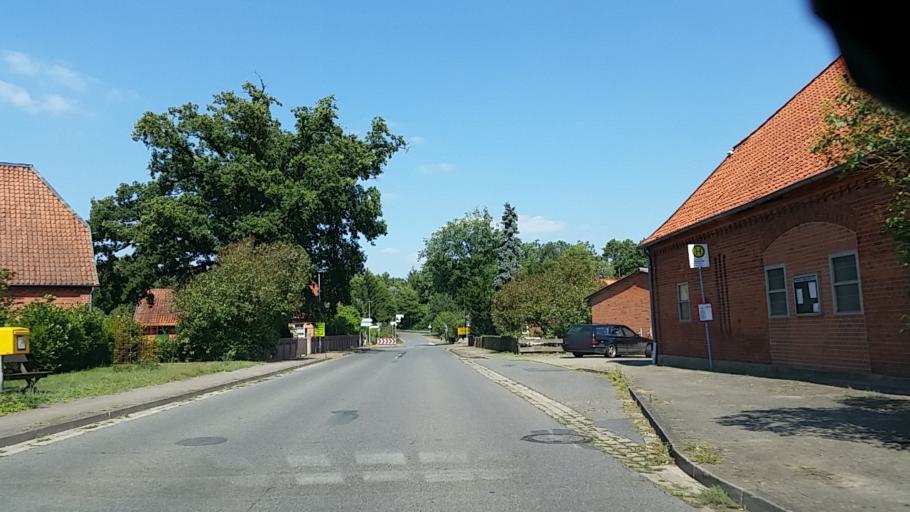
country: DE
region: Lower Saxony
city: Jelmstorf
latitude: 53.1074
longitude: 10.5432
